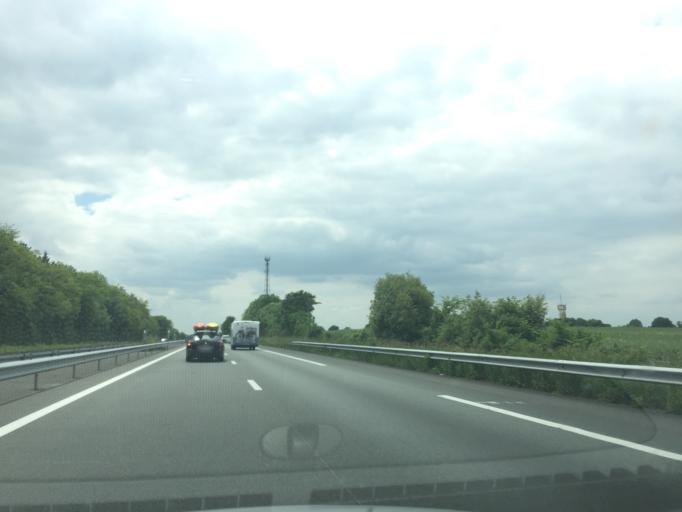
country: FR
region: Poitou-Charentes
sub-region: Departement des Deux-Sevres
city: Nanteuil
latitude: 46.3822
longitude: -0.2065
